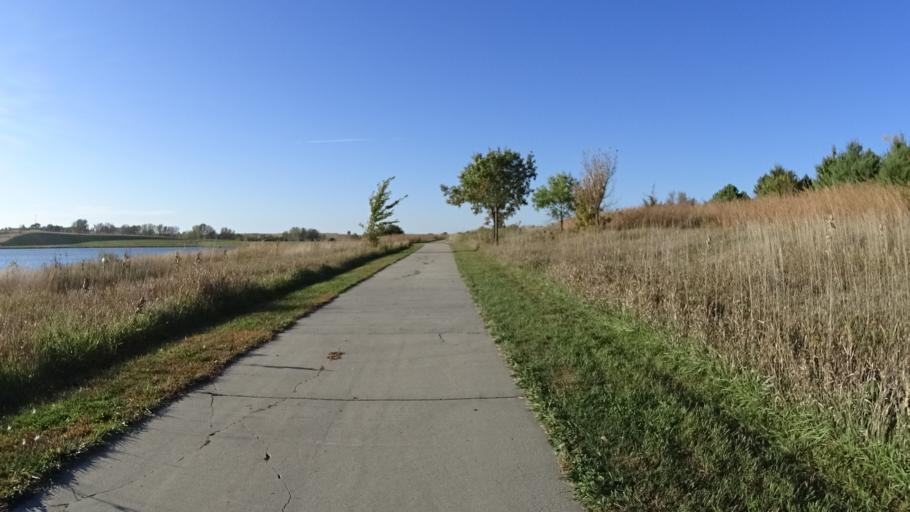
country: US
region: Nebraska
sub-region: Sarpy County
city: Papillion
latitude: 41.1419
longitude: -96.0650
